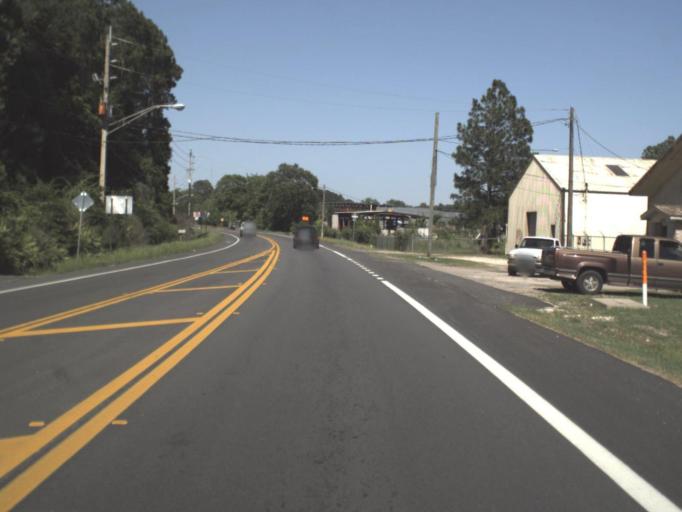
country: US
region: Florida
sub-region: Duval County
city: Jacksonville
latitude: 30.3203
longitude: -81.7928
